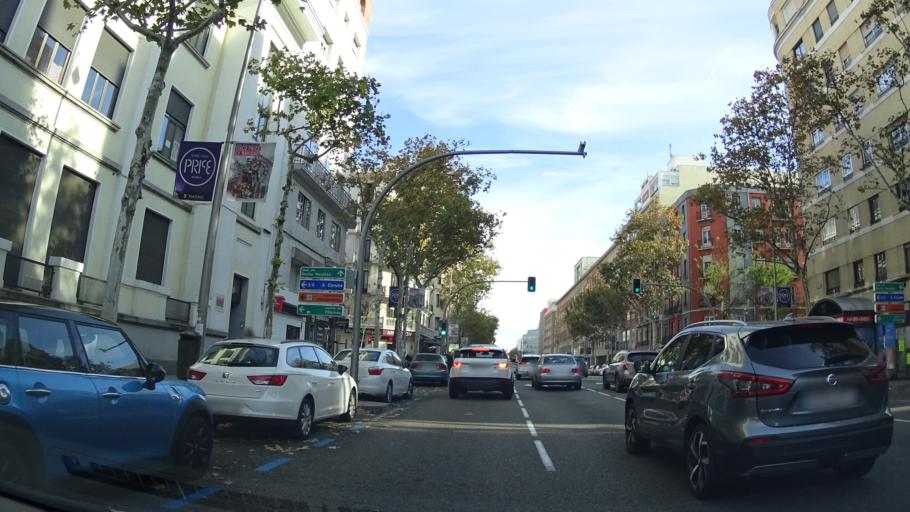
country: ES
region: Madrid
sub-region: Provincia de Madrid
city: Chamberi
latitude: 40.4389
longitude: -3.7088
